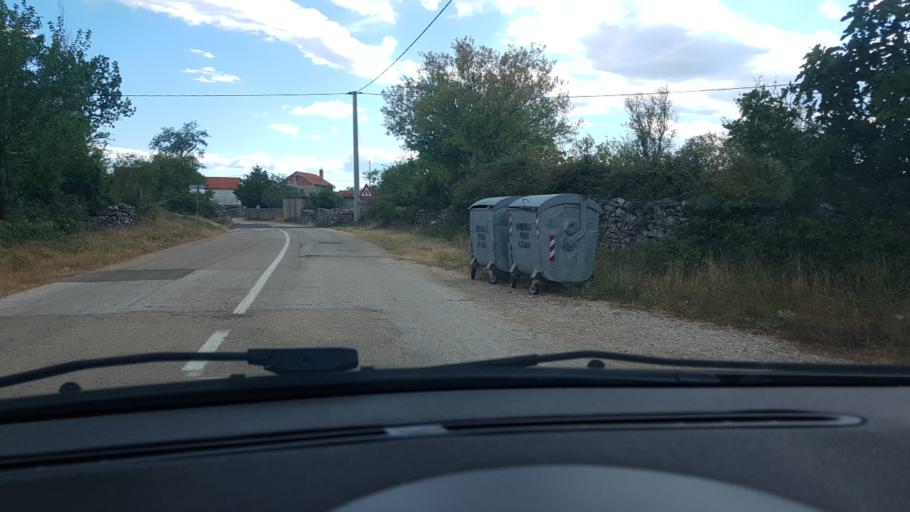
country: HR
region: Sibensko-Kniniska
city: Kistanje
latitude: 44.0565
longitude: 15.9261
